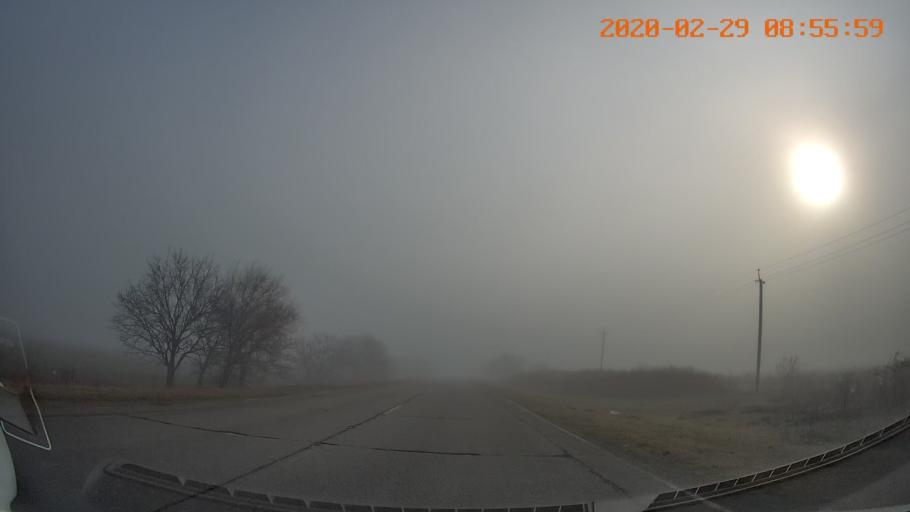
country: MD
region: Telenesti
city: Tiraspolul Nou
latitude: 46.9291
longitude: 29.6014
